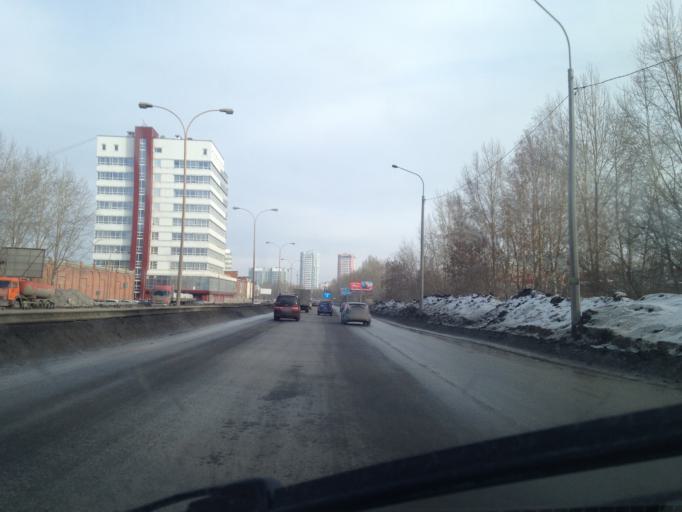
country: RU
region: Sverdlovsk
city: Yekaterinburg
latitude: 56.7879
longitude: 60.6218
